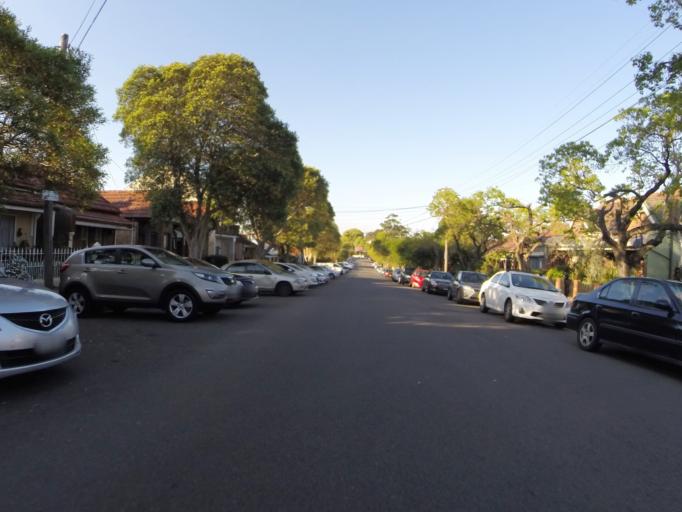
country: AU
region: New South Wales
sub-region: Marrickville
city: Marrickville
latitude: -33.9089
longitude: 151.1568
